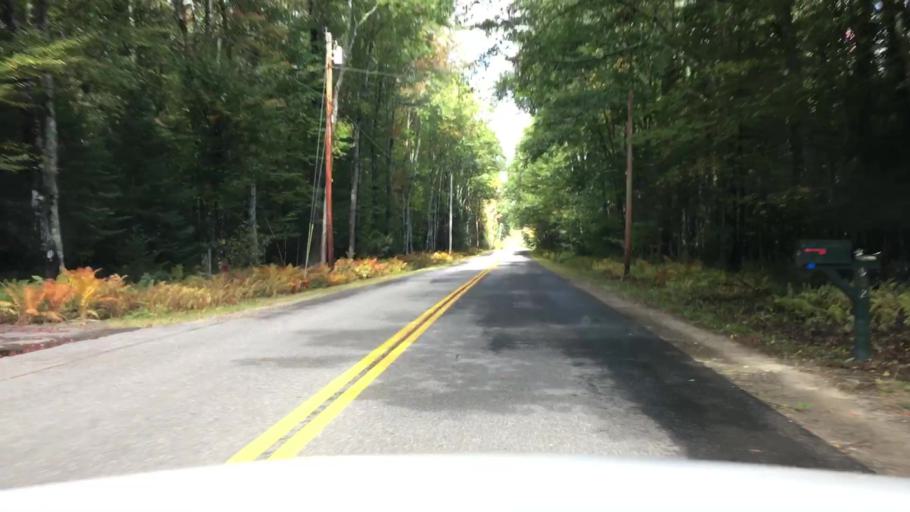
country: US
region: Maine
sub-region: Cumberland County
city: Brunswick
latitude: 43.9593
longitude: -69.8960
